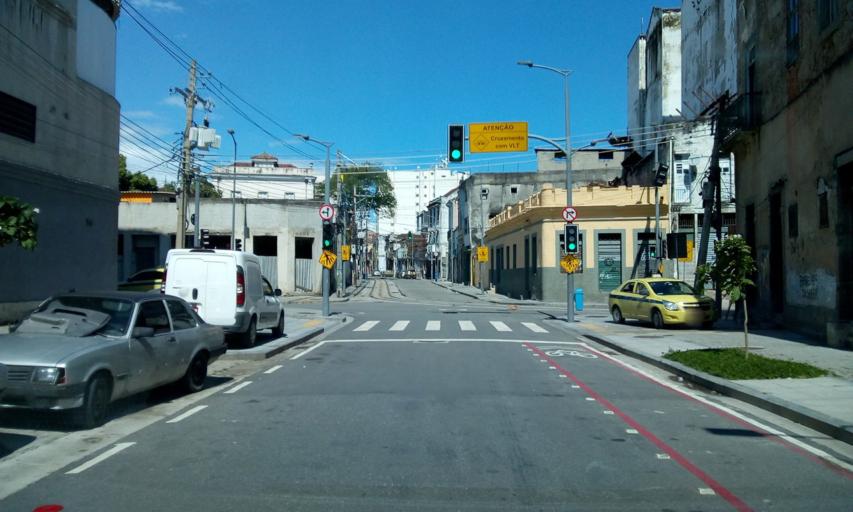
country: BR
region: Rio de Janeiro
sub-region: Rio De Janeiro
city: Rio de Janeiro
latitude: -22.8963
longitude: -43.1956
